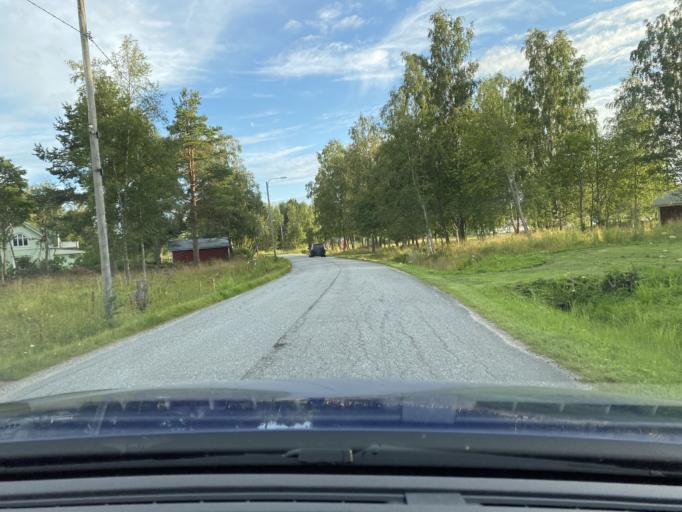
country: FI
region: Ostrobothnia
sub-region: Vaasa
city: Korsnaes
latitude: 62.9676
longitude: 21.1924
